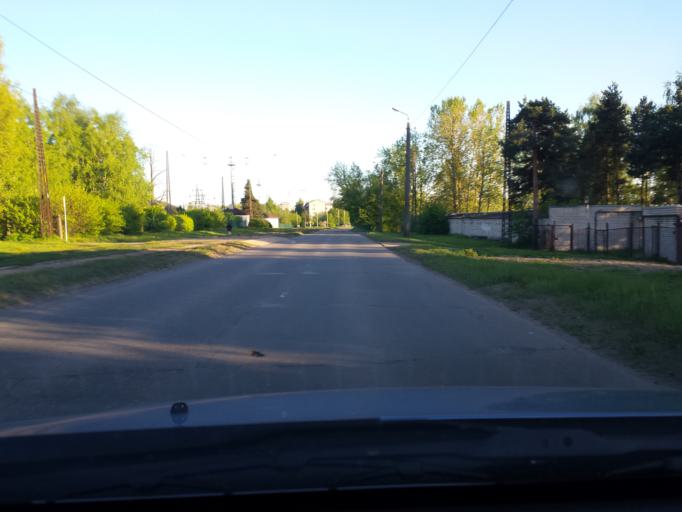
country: LV
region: Riga
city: Jaunciems
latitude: 57.0132
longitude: 24.1243
